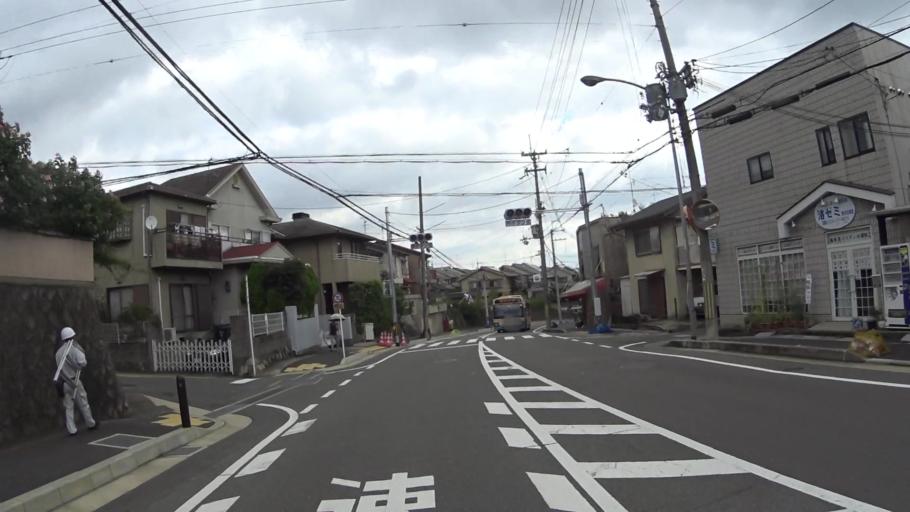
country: JP
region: Kyoto
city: Muko
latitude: 34.9517
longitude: 135.6940
